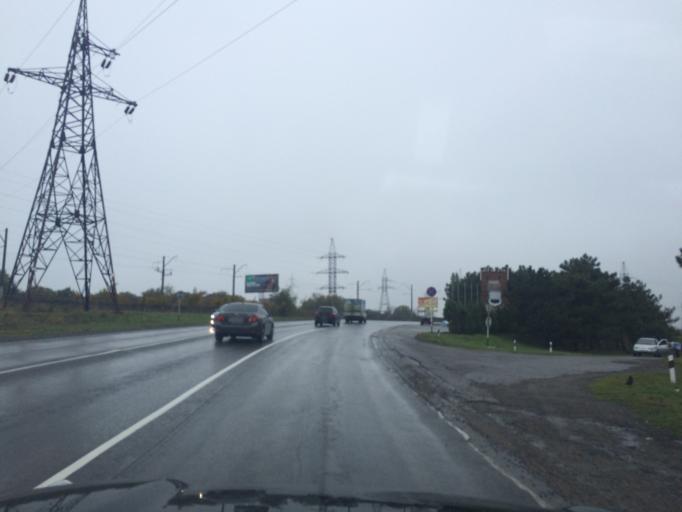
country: RU
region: Rostov
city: Azov
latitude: 47.0843
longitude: 39.4757
